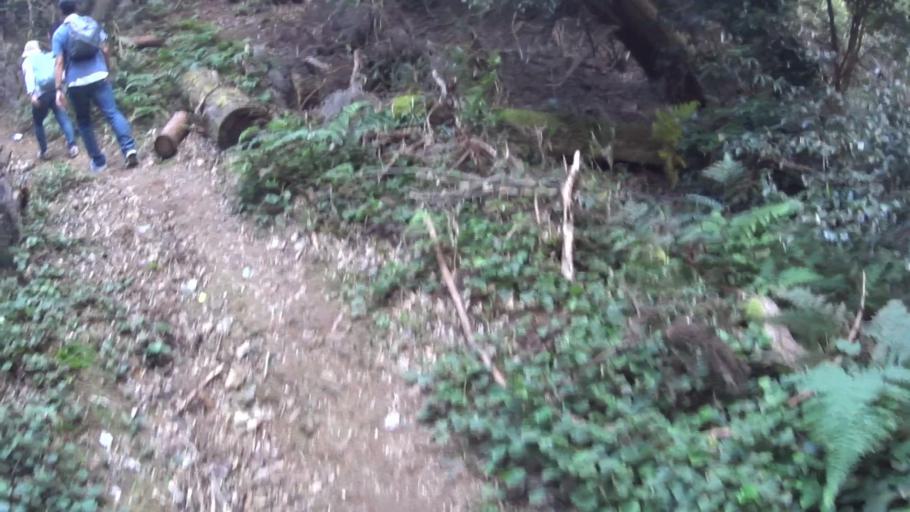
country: JP
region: Osaka
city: Kaizuka
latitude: 34.4772
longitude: 135.3097
